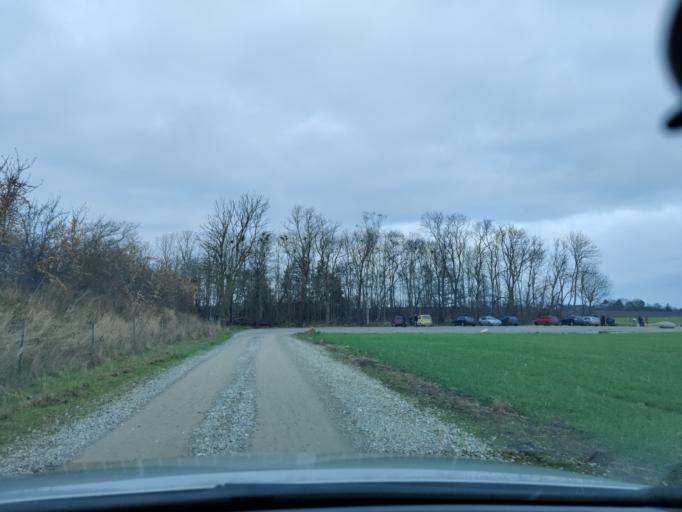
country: DK
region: South Denmark
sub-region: Kerteminde Kommune
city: Kerteminde
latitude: 55.4659
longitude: 10.6544
